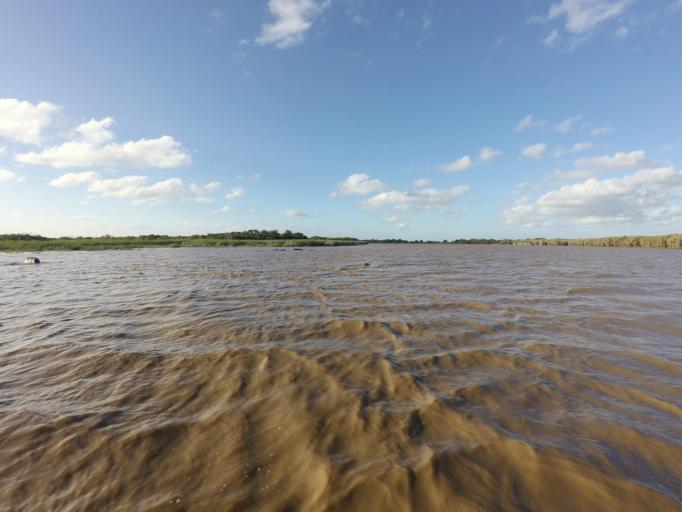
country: ZA
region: KwaZulu-Natal
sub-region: uMkhanyakude District Municipality
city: Mtubatuba
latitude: -28.3500
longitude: 32.4093
